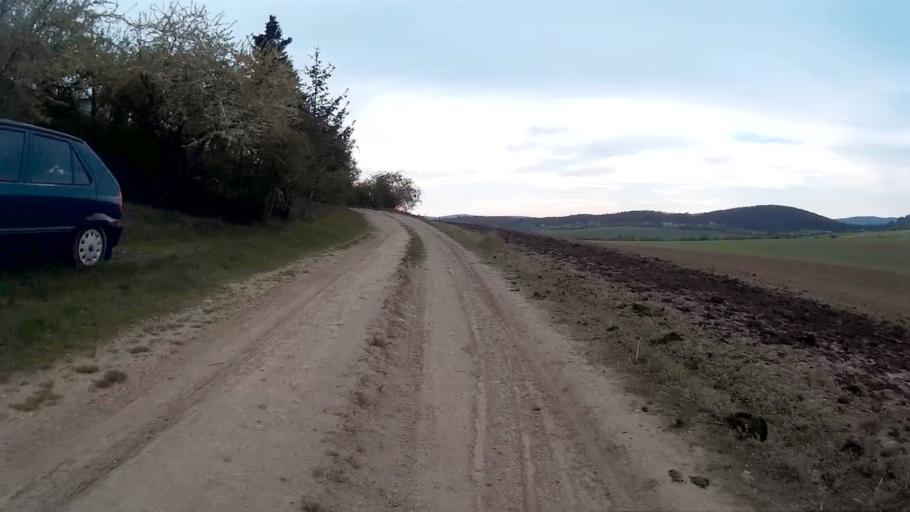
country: CZ
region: South Moravian
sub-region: Mesto Brno
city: Mokra Hora
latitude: 49.2339
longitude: 16.5515
